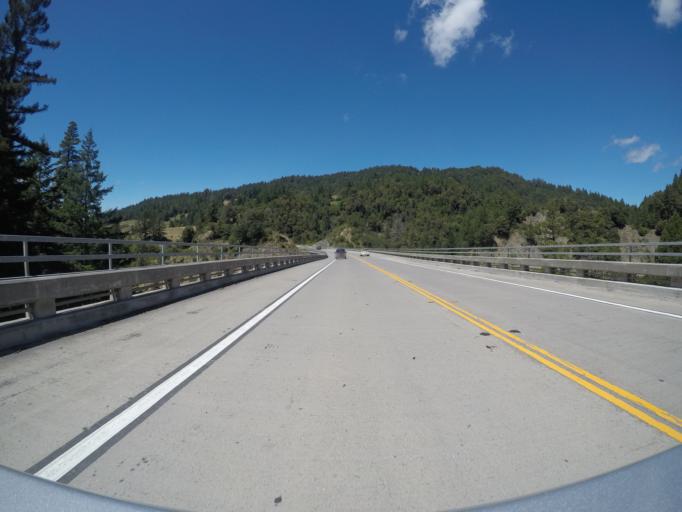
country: US
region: California
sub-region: Humboldt County
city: Redway
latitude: 39.9264
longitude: -123.7610
